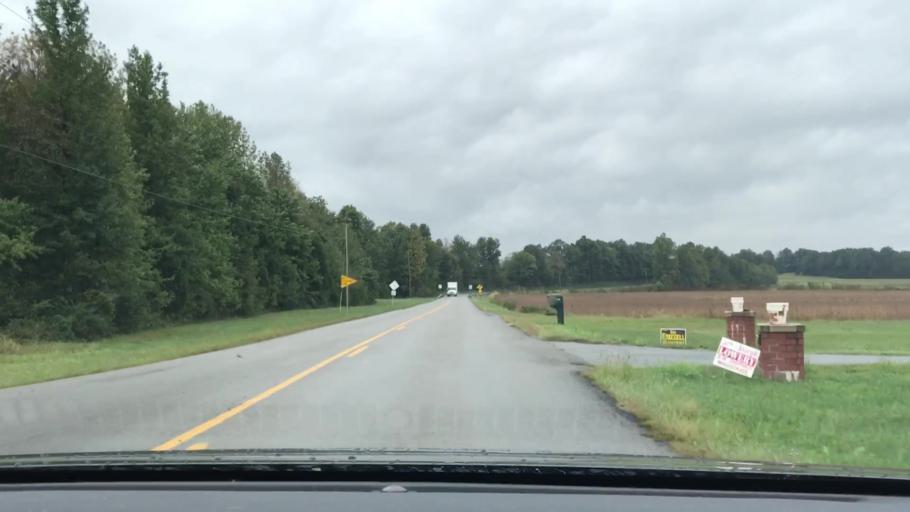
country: US
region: Kentucky
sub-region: McLean County
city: Calhoun
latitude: 37.4516
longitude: -87.2362
